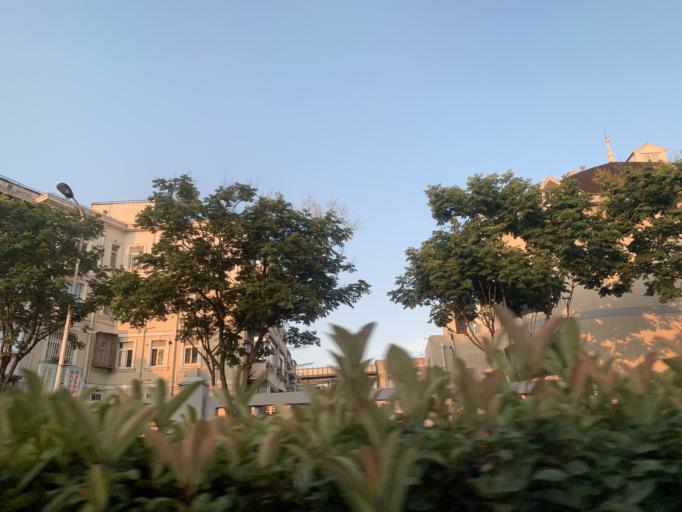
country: CN
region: Shanghai Shi
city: Huamu
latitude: 31.1856
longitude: 121.5503
